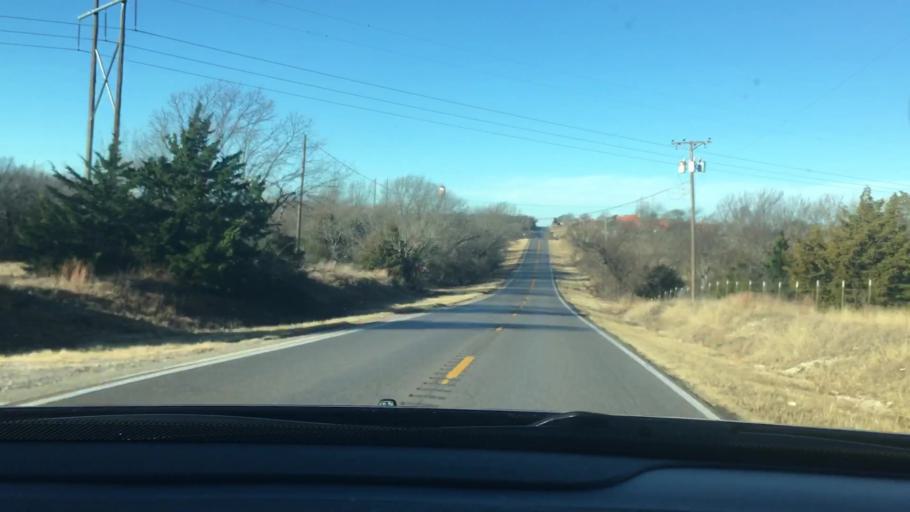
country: US
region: Oklahoma
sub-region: Murray County
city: Sulphur
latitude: 34.5109
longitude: -96.9423
